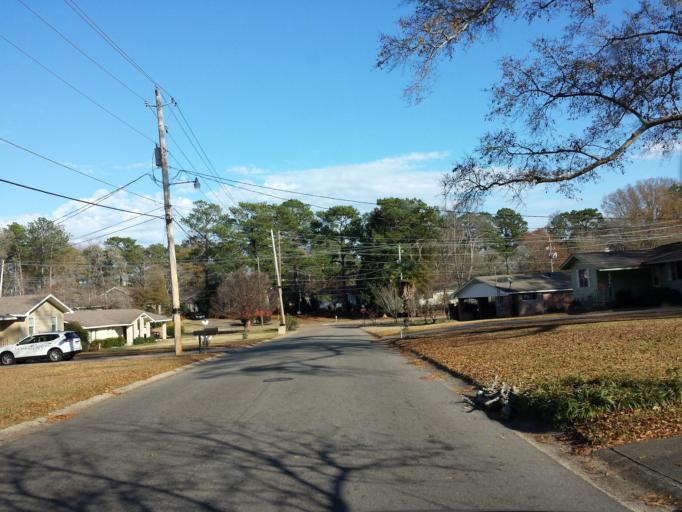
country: US
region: Mississippi
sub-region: Lamar County
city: West Hattiesburg
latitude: 31.3114
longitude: -89.3322
